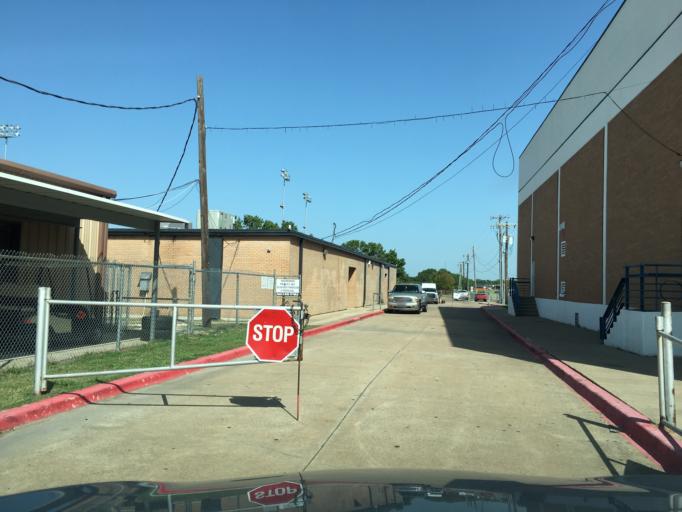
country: US
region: Texas
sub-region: Dallas County
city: Garland
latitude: 32.8723
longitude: -96.6193
